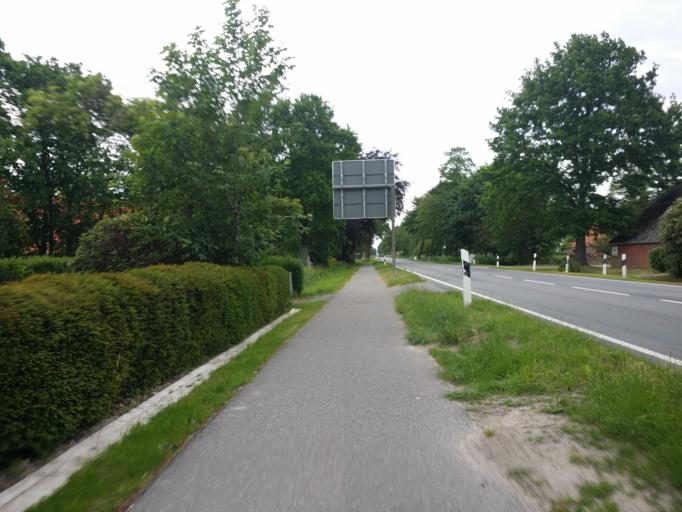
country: DE
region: Lower Saxony
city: Wittmund
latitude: 53.5875
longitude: 7.7841
